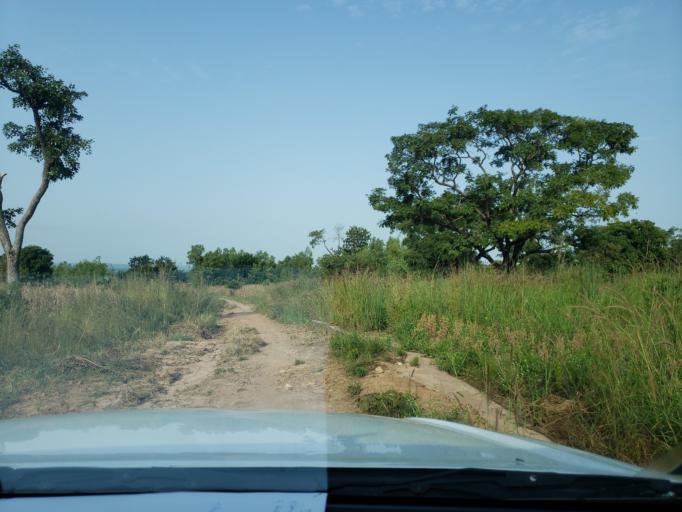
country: TG
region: Kara
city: Bafilo
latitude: 9.4108
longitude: 1.1828
